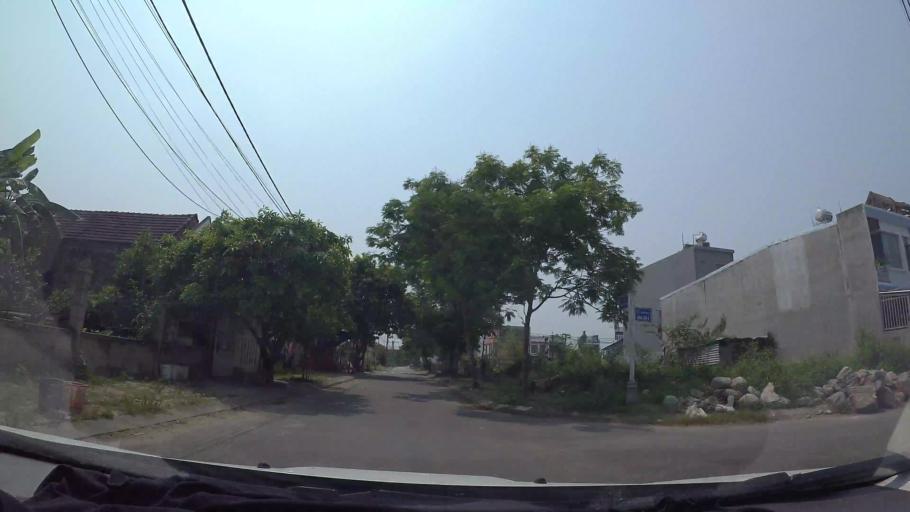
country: VN
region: Da Nang
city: Cam Le
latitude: 15.9982
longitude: 108.2061
